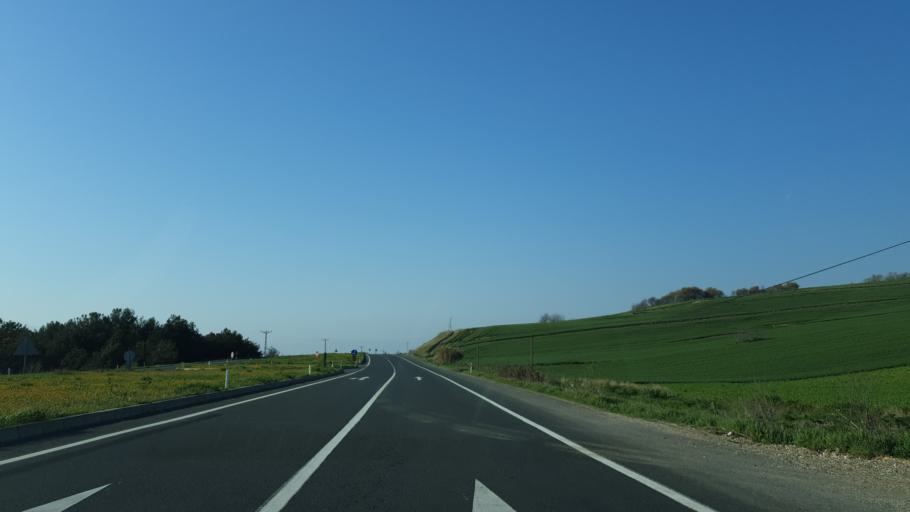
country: TR
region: Tekirdag
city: Corlu
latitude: 41.0475
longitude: 27.7336
